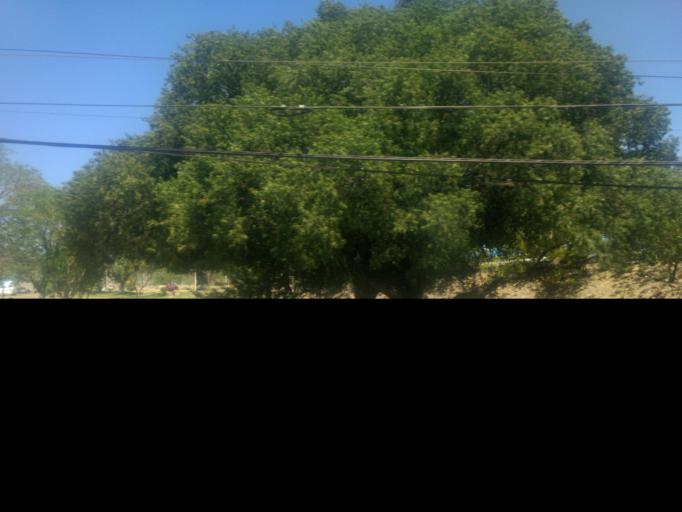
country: MX
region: Jalisco
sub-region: Tlajomulco de Zuniga
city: Santa Cruz de las Flores
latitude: 20.4904
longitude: -103.4904
